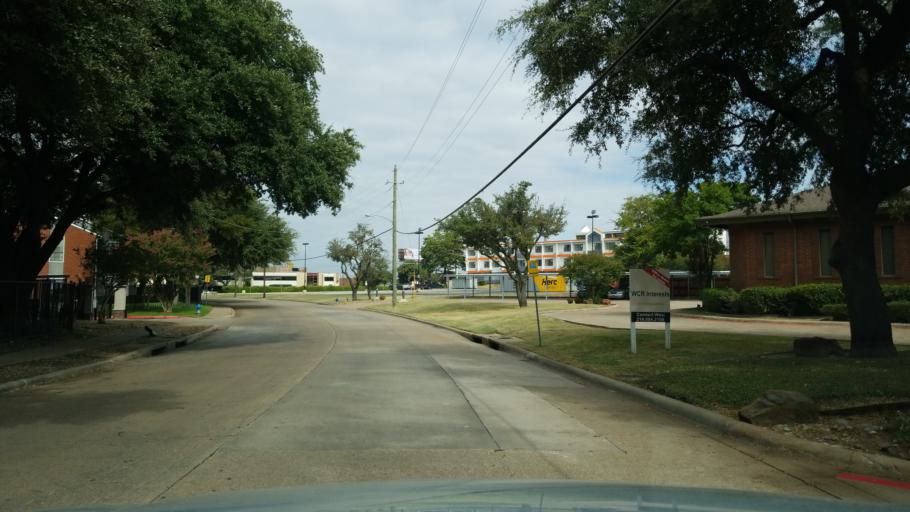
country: US
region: Texas
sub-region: Dallas County
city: Garland
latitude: 32.8730
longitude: -96.6854
